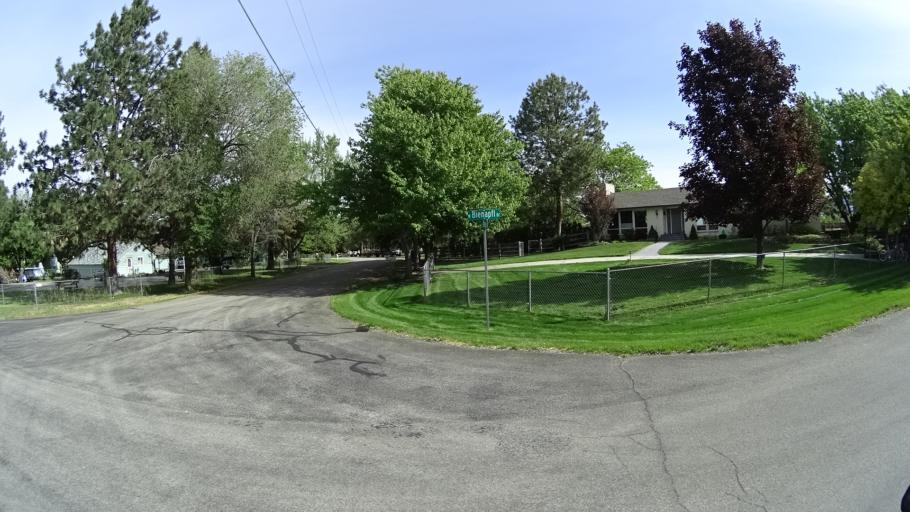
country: US
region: Idaho
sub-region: Ada County
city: Garden City
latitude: 43.5654
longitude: -116.2962
